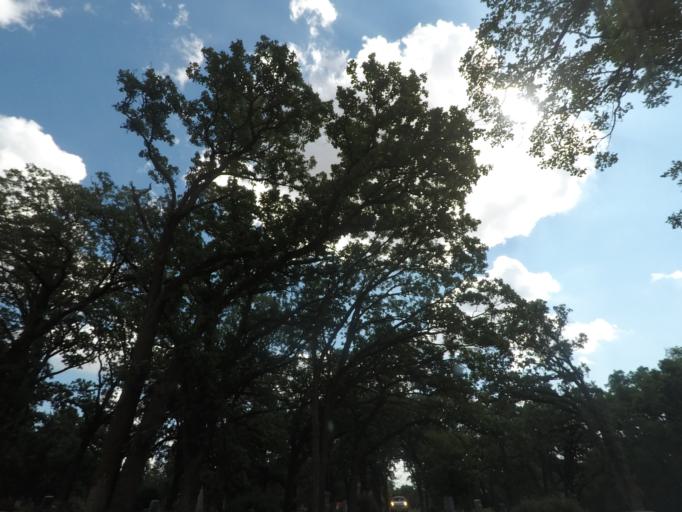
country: US
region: Iowa
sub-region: Story County
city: Nevada
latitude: 42.0219
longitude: -93.4637
